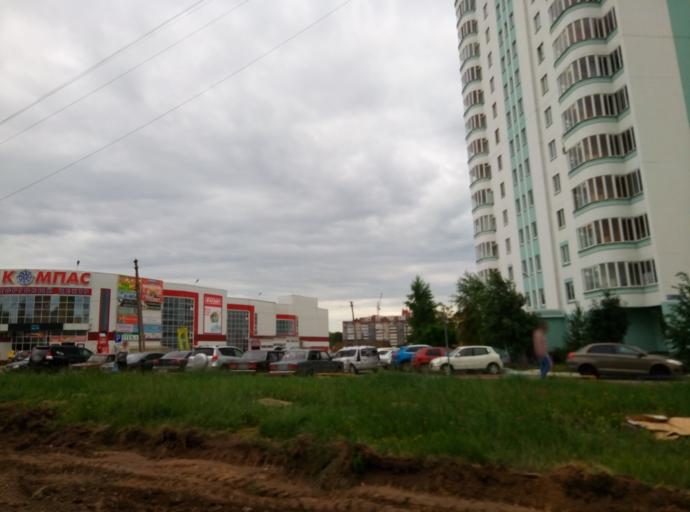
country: RU
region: Kursk
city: Kursk
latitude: 51.7269
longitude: 36.1402
